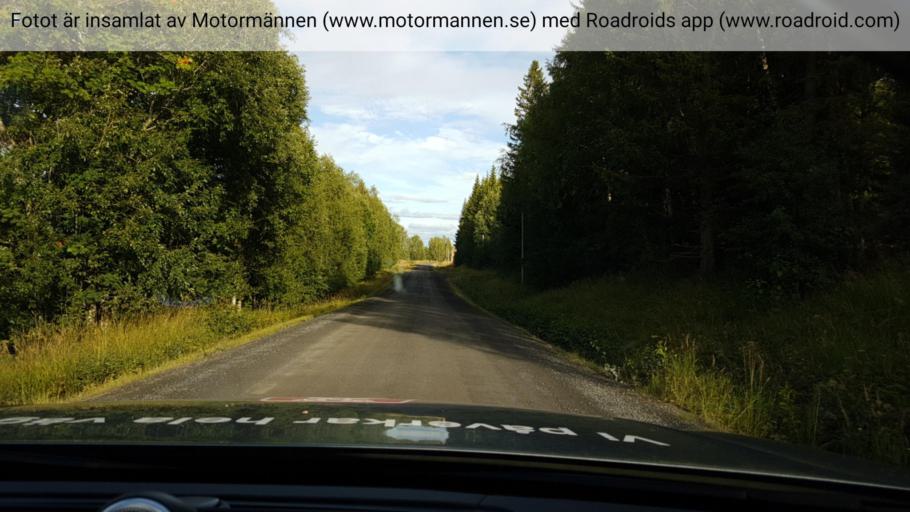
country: SE
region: Jaemtland
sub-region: Stroemsunds Kommun
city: Stroemsund
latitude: 64.1418
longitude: 15.7279
